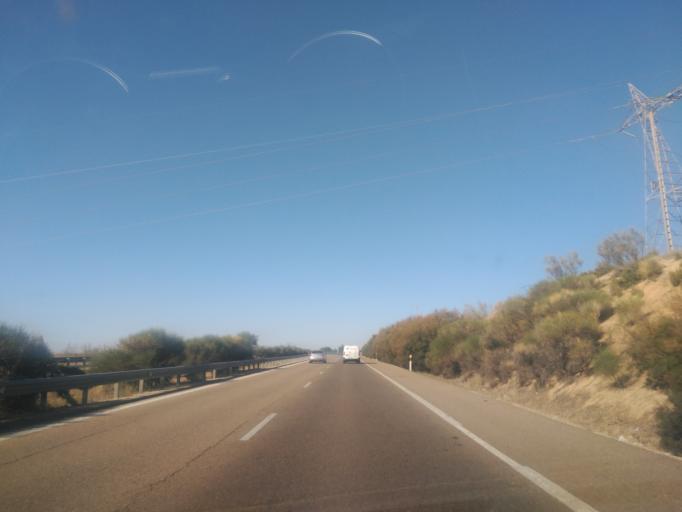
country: ES
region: Castille and Leon
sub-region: Provincia de Valladolid
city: Cisterniga
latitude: 41.5973
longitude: -4.6447
